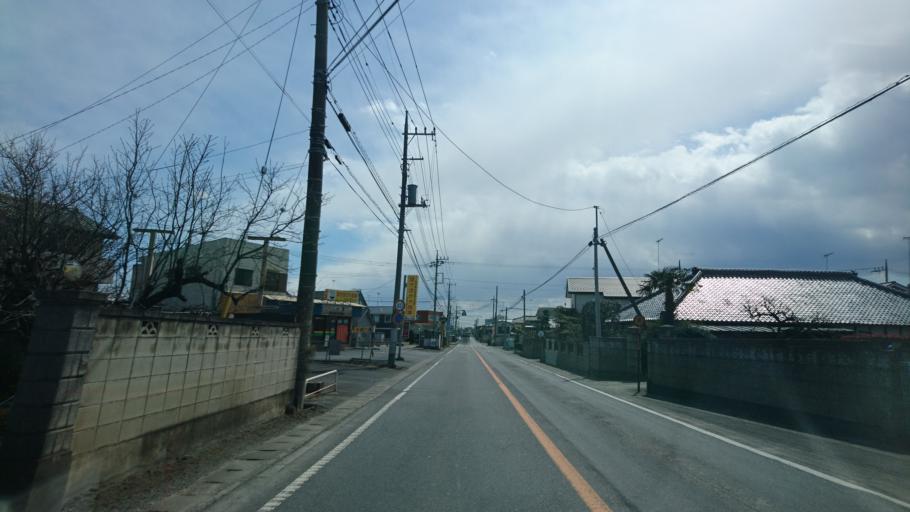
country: JP
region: Ibaraki
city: Yuki
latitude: 36.2907
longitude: 139.9140
